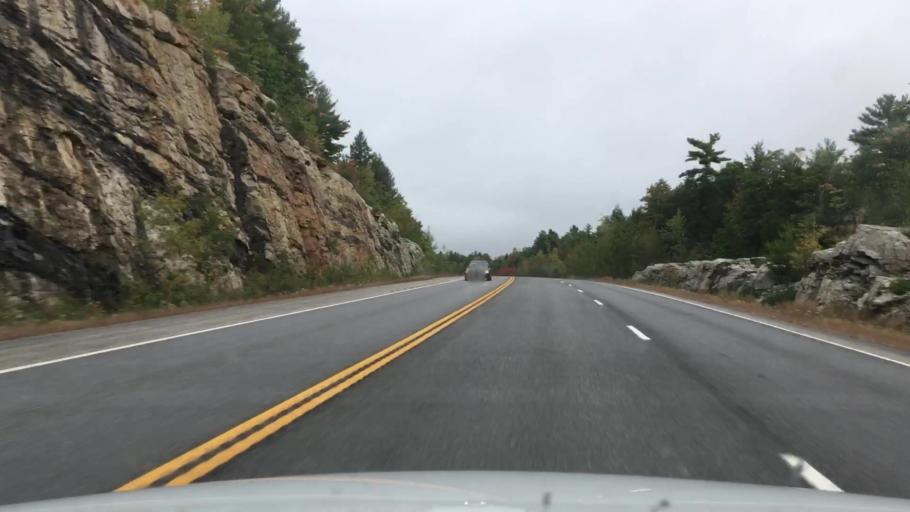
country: US
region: Maine
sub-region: Cumberland County
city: New Gloucester
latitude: 43.9525
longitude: -70.3505
